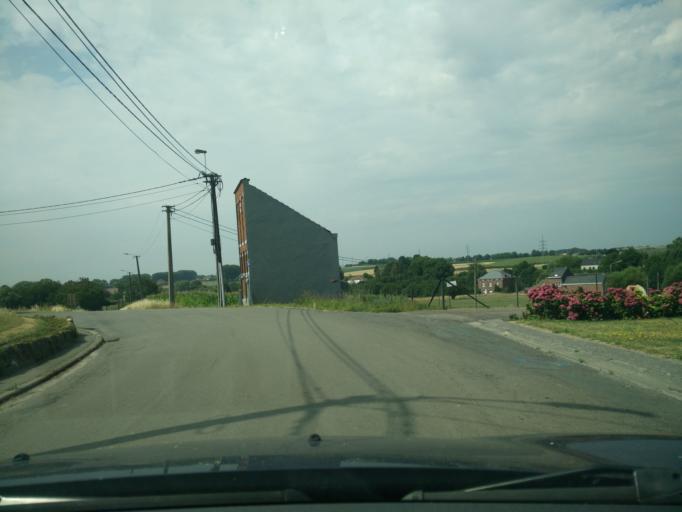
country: BE
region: Wallonia
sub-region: Province du Hainaut
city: Braine-le-Comte
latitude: 50.6419
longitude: 4.1719
